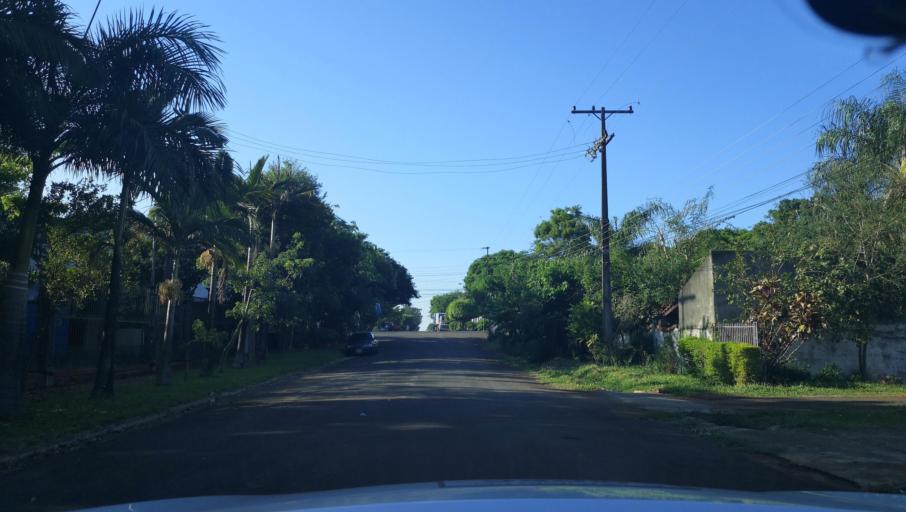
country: PY
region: Itapua
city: Carmen del Parana
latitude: -27.1557
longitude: -56.2451
